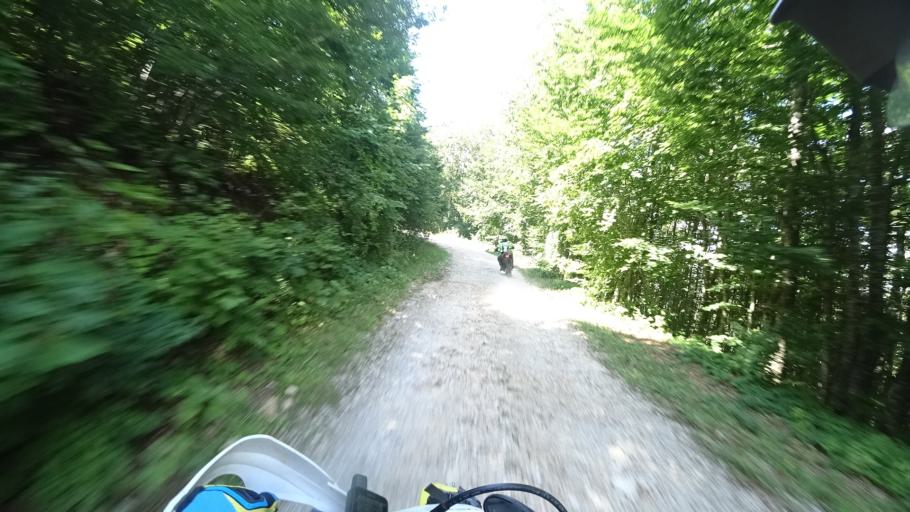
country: HR
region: Zadarska
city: Gracac
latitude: 44.4523
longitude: 15.9789
